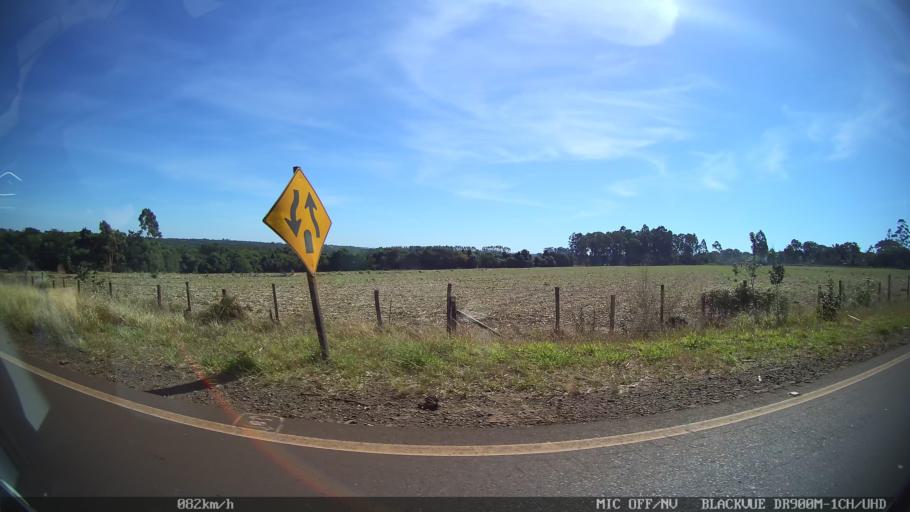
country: BR
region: Sao Paulo
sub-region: Franca
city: Franca
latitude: -20.5572
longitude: -47.4997
